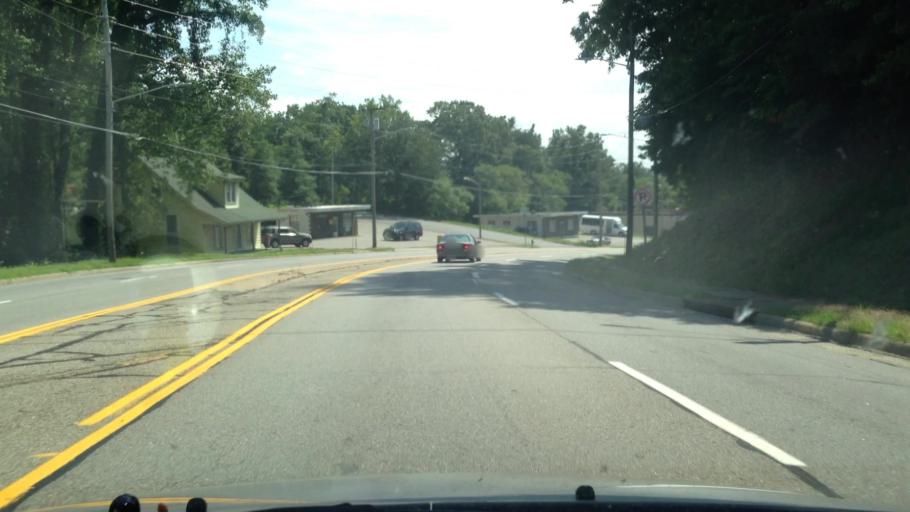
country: US
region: Virginia
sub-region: City of Martinsville
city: Martinsville
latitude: 36.6765
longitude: -79.8758
